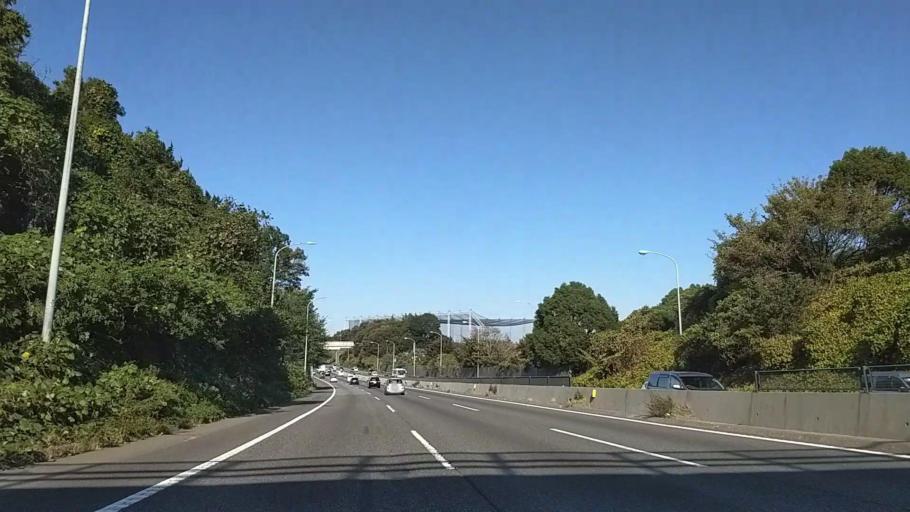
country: JP
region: Kanagawa
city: Minami-rinkan
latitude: 35.4745
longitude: 139.5292
